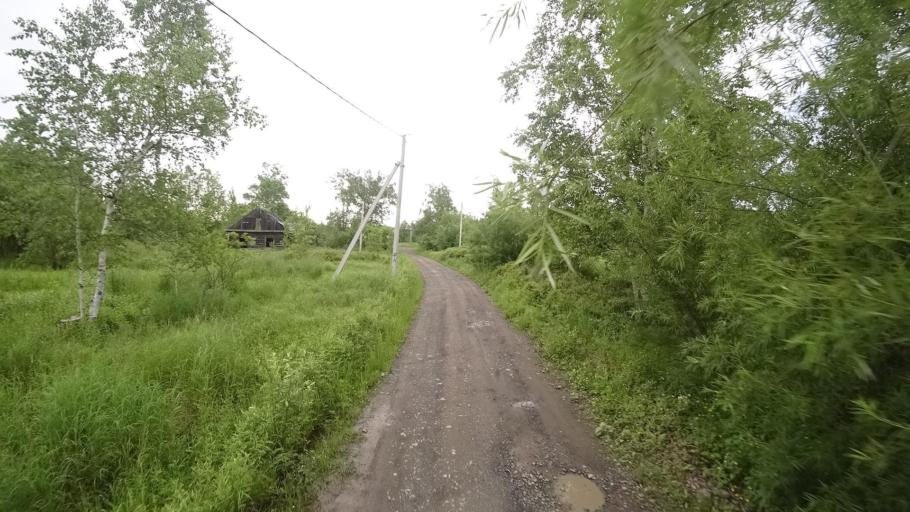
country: RU
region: Khabarovsk Krai
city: Amursk
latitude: 49.9032
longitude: 136.1367
